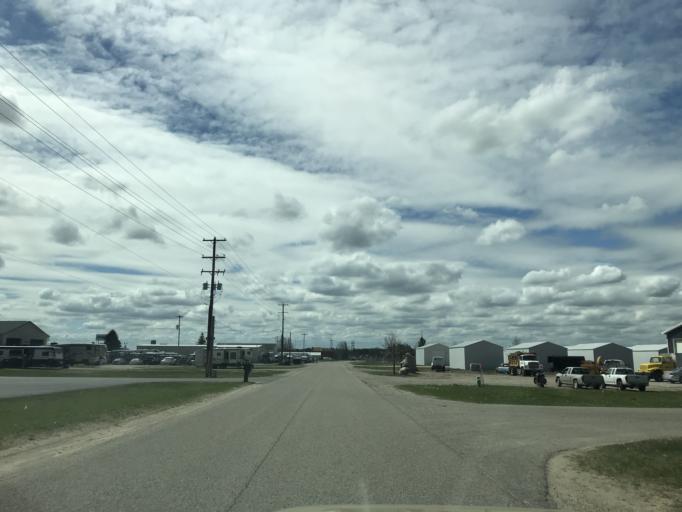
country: US
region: Michigan
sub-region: Otsego County
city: Gaylord
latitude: 45.0332
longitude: -84.6918
